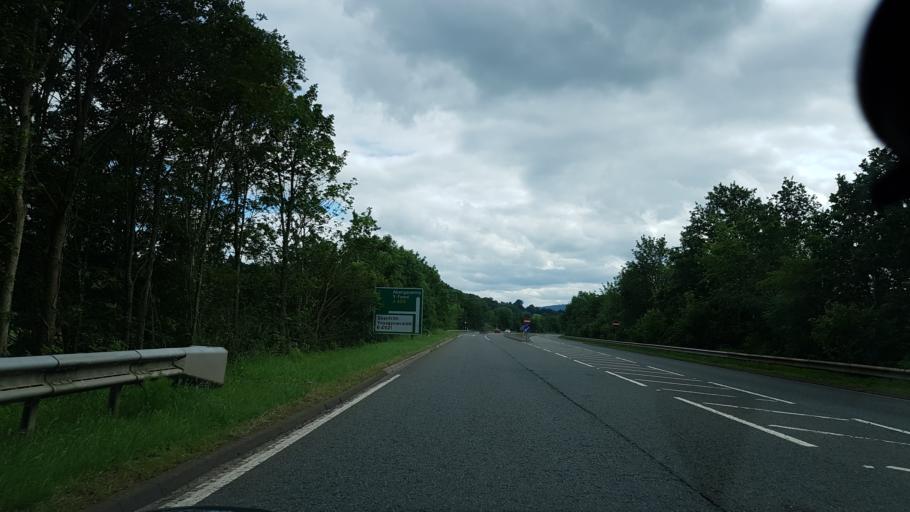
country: GB
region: Wales
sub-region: Monmouthshire
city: Abergavenny
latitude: 51.8366
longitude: -2.9997
